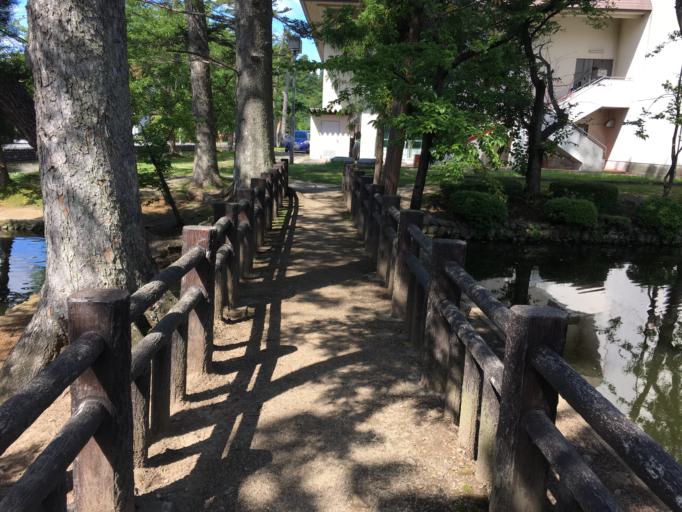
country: JP
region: Yamagata
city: Yonezawa
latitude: 37.9075
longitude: 140.1038
